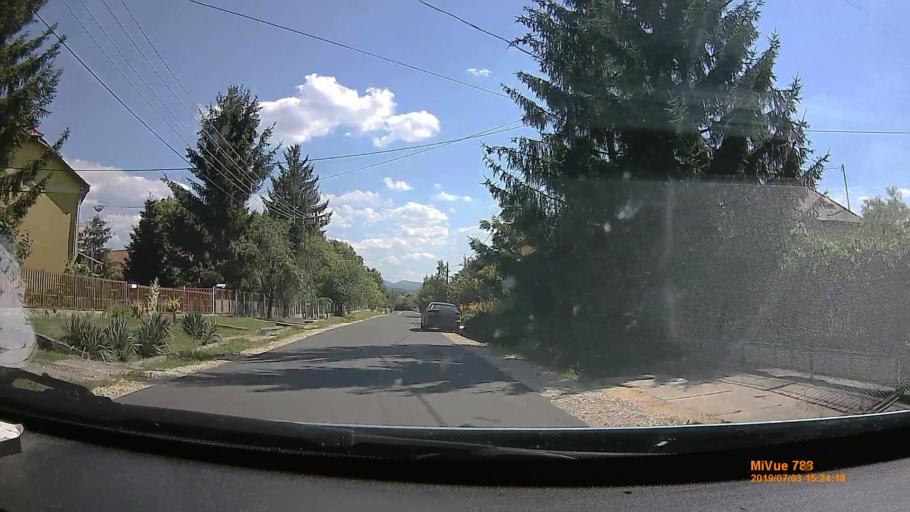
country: HU
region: Borsod-Abauj-Zemplen
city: Farkaslyuk
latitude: 48.1942
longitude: 20.3925
